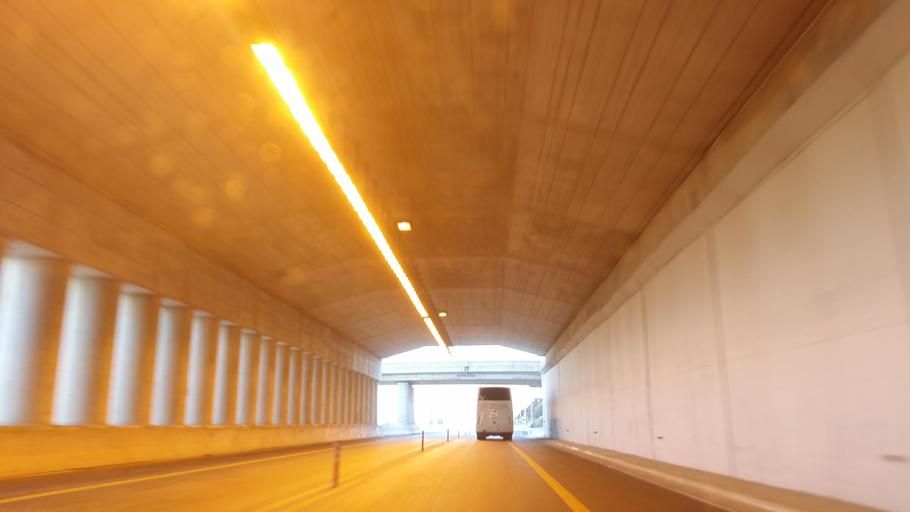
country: GR
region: Peloponnese
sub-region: Nomos Korinthias
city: Xylokastro
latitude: 38.0717
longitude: 22.6326
